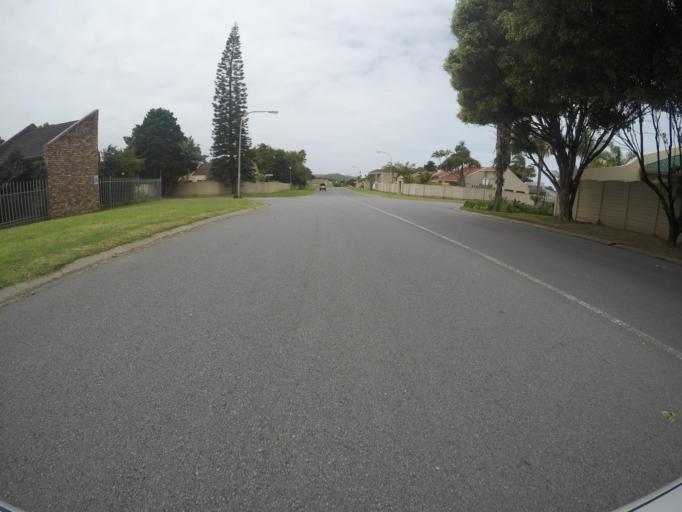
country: ZA
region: Eastern Cape
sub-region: Buffalo City Metropolitan Municipality
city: East London
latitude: -32.9783
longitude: 27.9508
